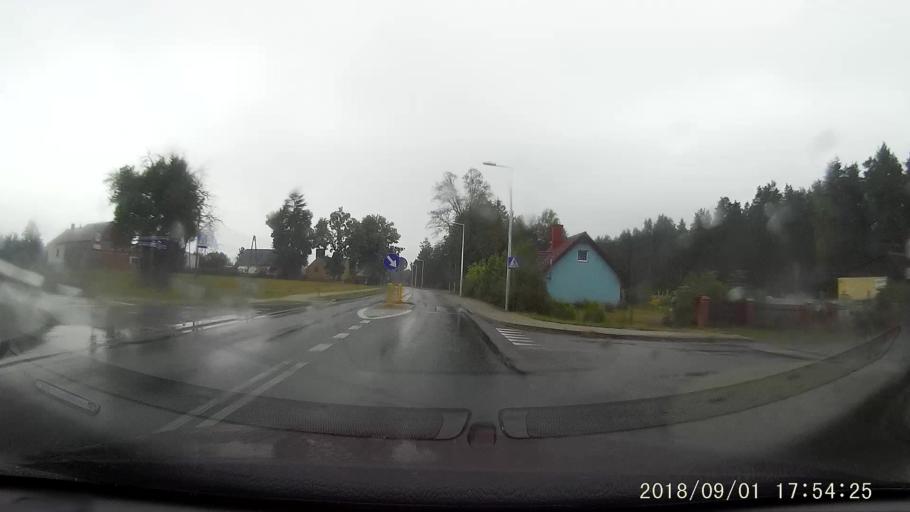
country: PL
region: Lubusz
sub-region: Powiat zaganski
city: Ilowa
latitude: 51.4690
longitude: 15.1994
